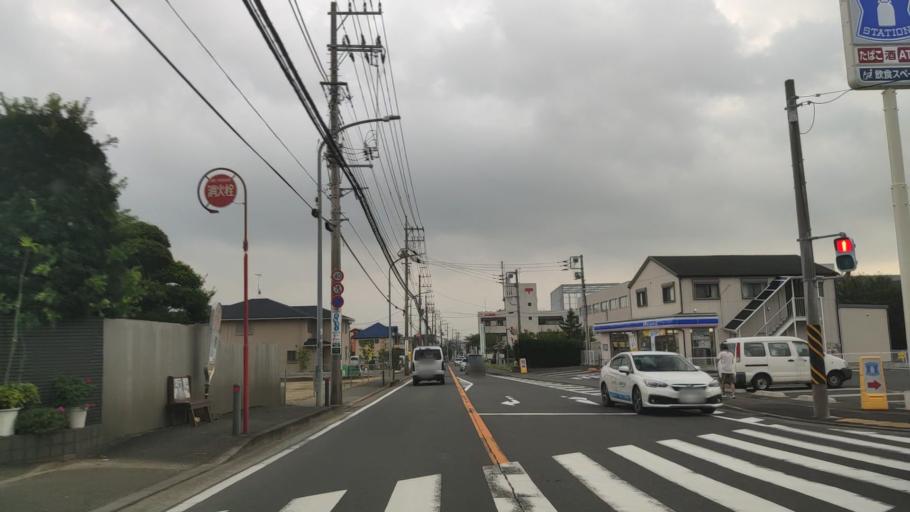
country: JP
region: Kanagawa
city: Minami-rinkan
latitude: 35.4232
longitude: 139.5016
